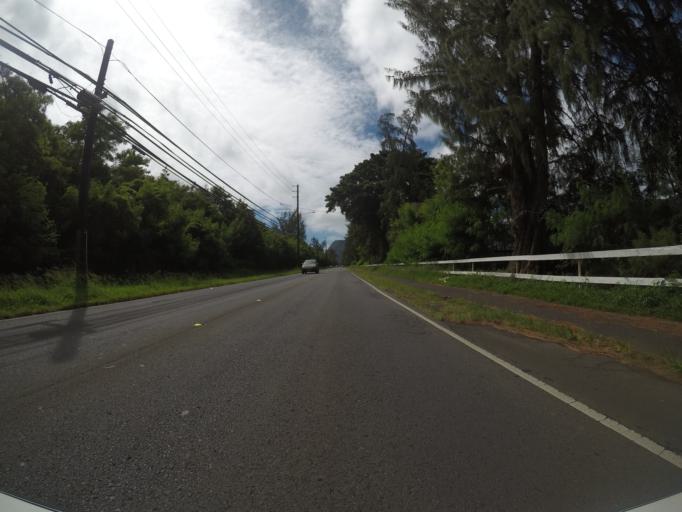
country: US
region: Hawaii
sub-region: Honolulu County
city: Waimanalo
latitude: 21.3447
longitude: -157.7096
